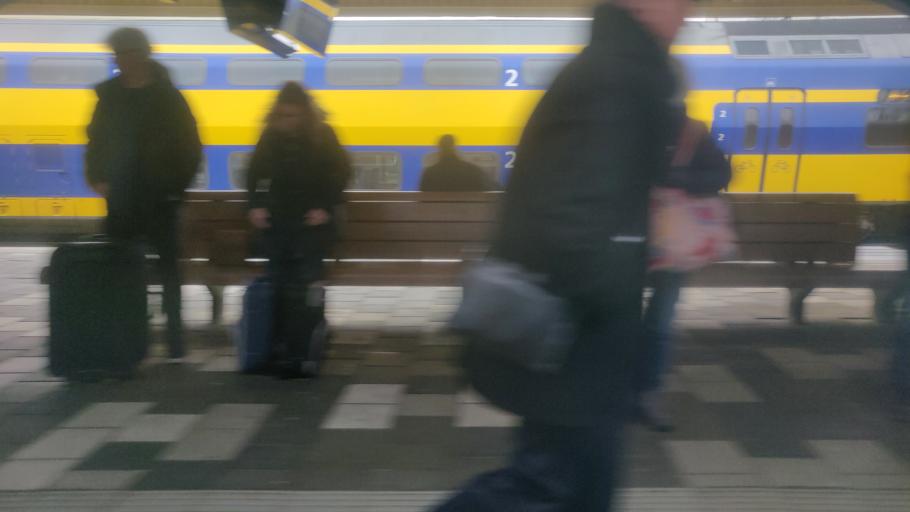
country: NL
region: North Holland
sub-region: Gemeente Alkmaar
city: Alkmaar
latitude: 52.6380
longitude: 4.7400
